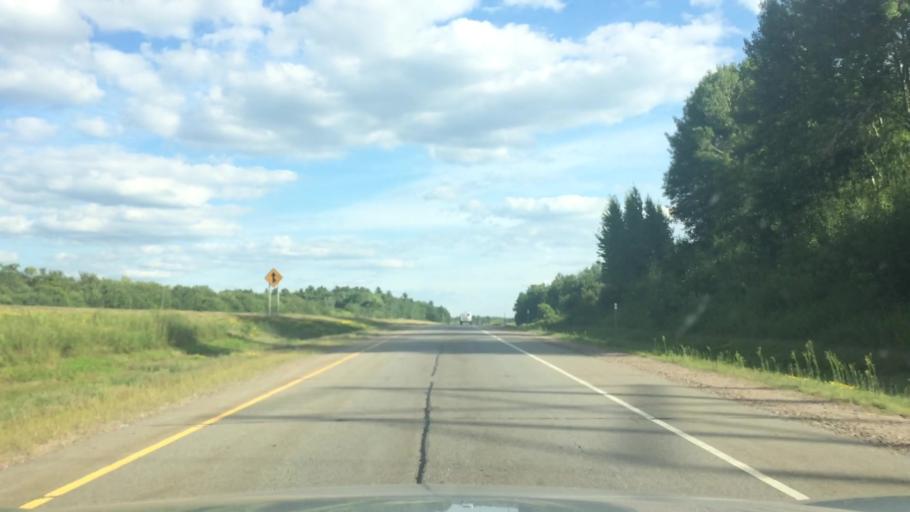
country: US
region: Wisconsin
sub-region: Lincoln County
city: Merrill
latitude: 45.1752
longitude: -89.6474
